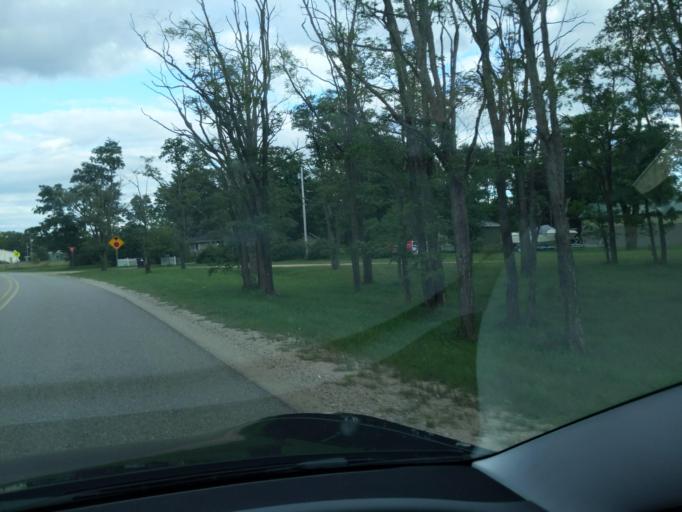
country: US
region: Michigan
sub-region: Kalkaska County
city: Rapid City
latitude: 44.8347
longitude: -85.2859
